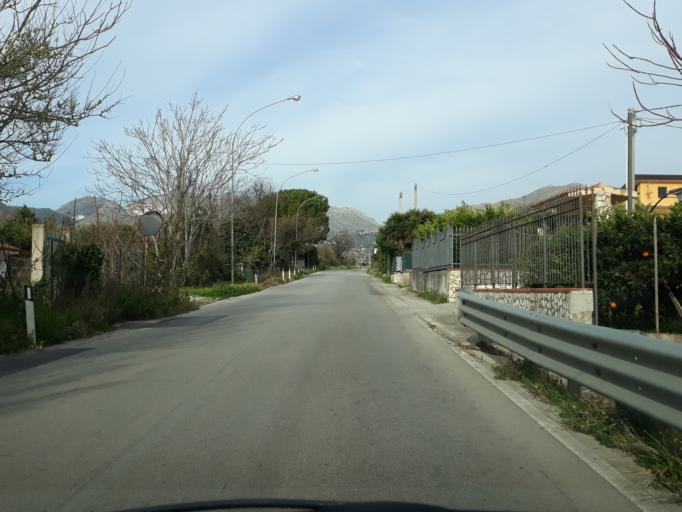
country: IT
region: Sicily
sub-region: Palermo
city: Borgetto
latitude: 38.0650
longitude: 13.1461
